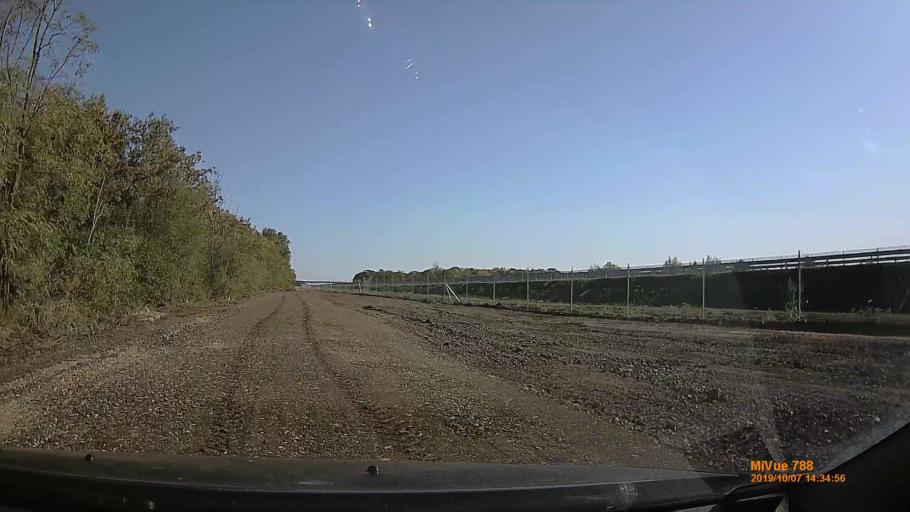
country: HU
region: Jasz-Nagykun-Szolnok
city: Kunszentmarton
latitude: 46.8596
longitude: 20.3054
